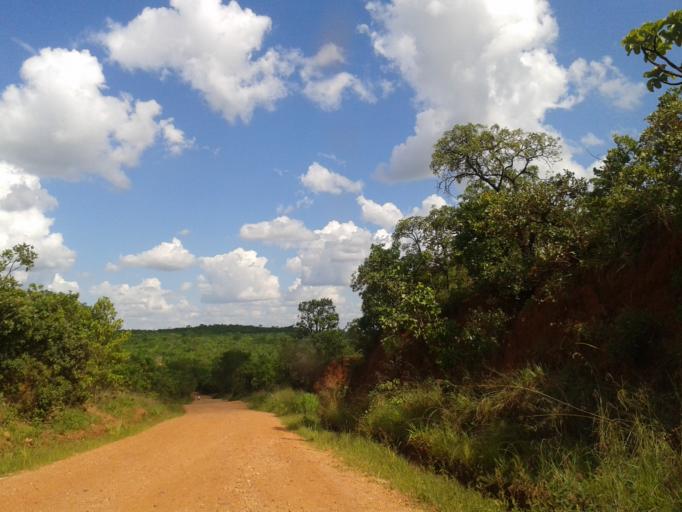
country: BR
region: Minas Gerais
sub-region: Campina Verde
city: Campina Verde
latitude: -19.3269
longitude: -49.7965
